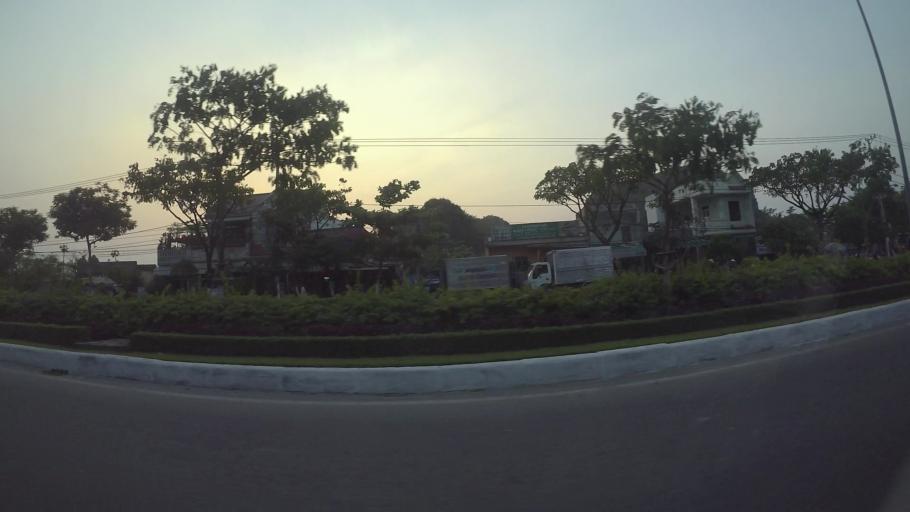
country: VN
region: Da Nang
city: Ngu Hanh Son
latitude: 15.9975
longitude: 108.2594
